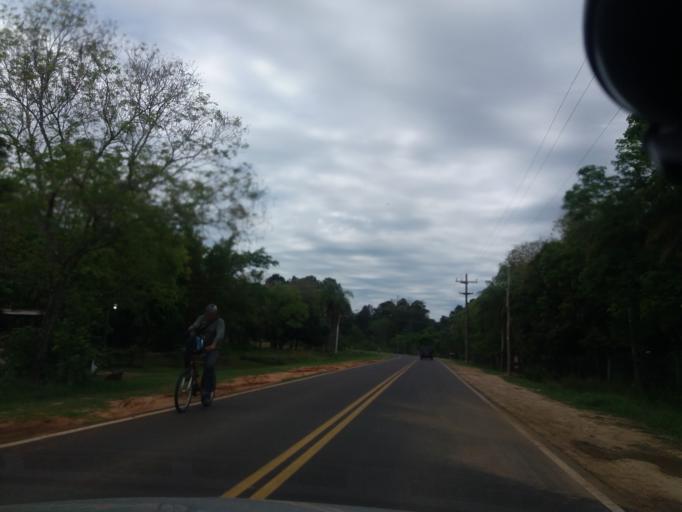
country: AR
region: Corrientes
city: Riachuelo
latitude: -27.4580
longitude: -58.7060
